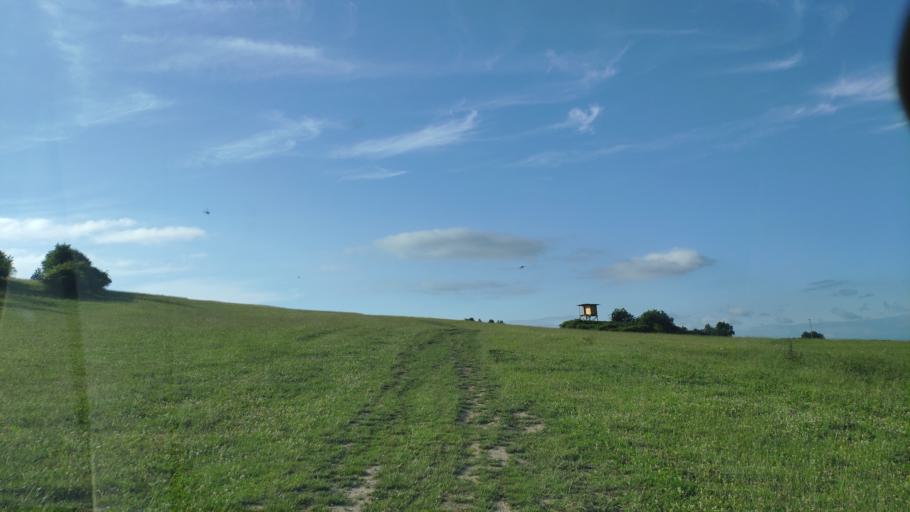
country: SK
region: Presovsky
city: Vranov nad Topl'ou
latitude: 48.8210
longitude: 21.5885
